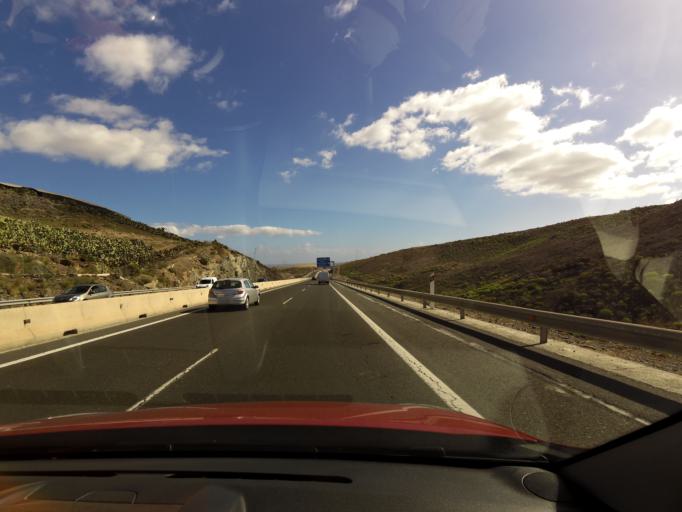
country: ES
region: Canary Islands
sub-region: Provincia de Las Palmas
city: Maspalomas
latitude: 27.7660
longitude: -15.6300
